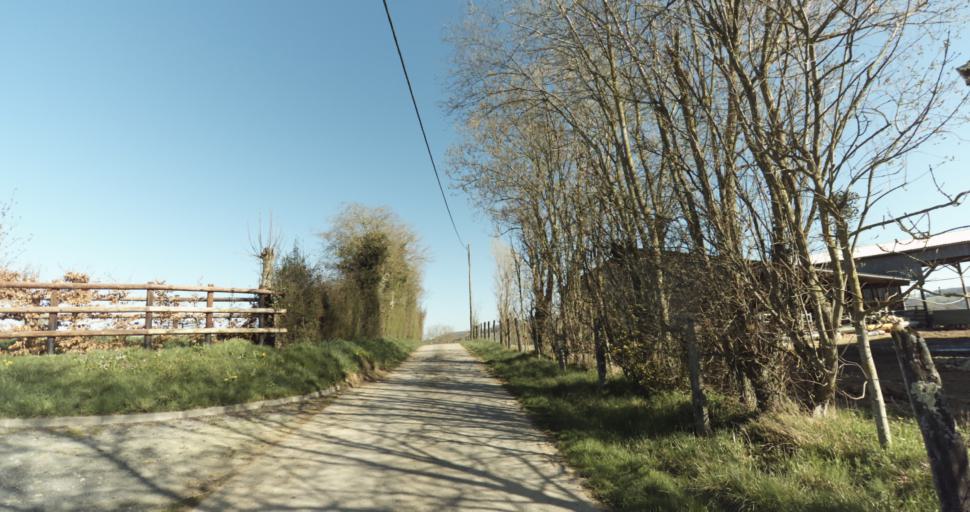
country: FR
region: Lower Normandy
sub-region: Departement du Calvados
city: Saint-Pierre-sur-Dives
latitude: 48.9672
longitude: 0.0390
